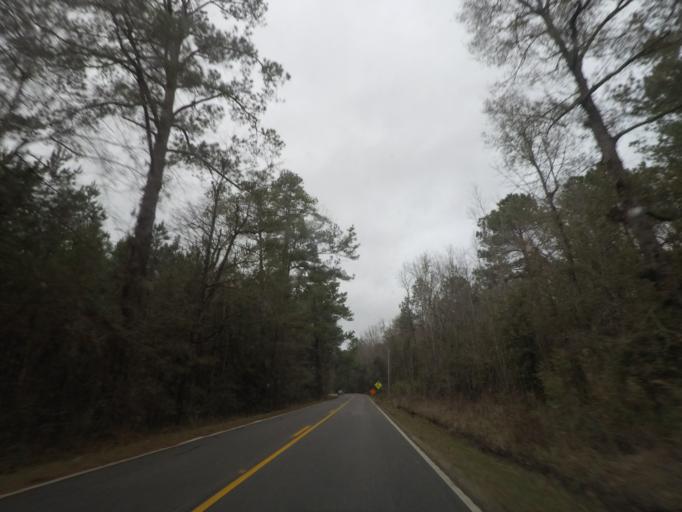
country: US
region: South Carolina
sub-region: Colleton County
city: Walterboro
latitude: 32.9103
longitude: -80.5204
